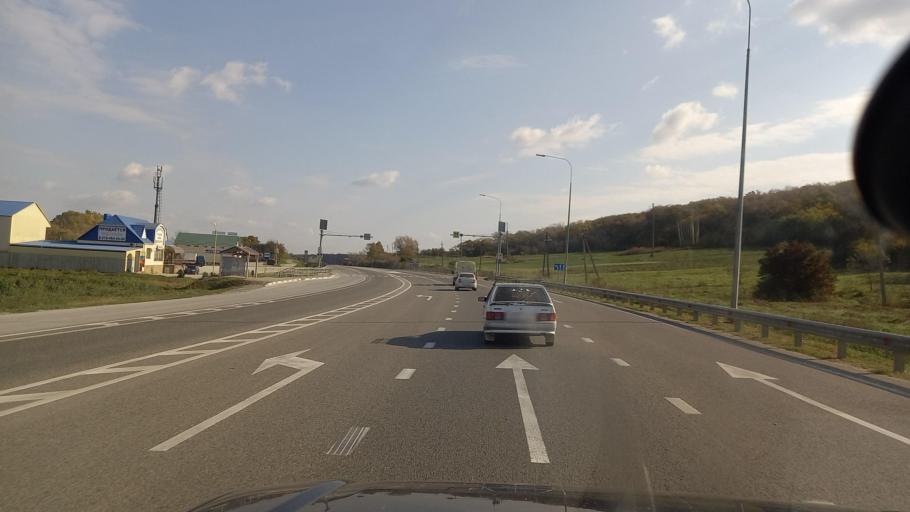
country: RU
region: Krasnodarskiy
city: Krymsk
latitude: 44.8739
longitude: 37.9210
